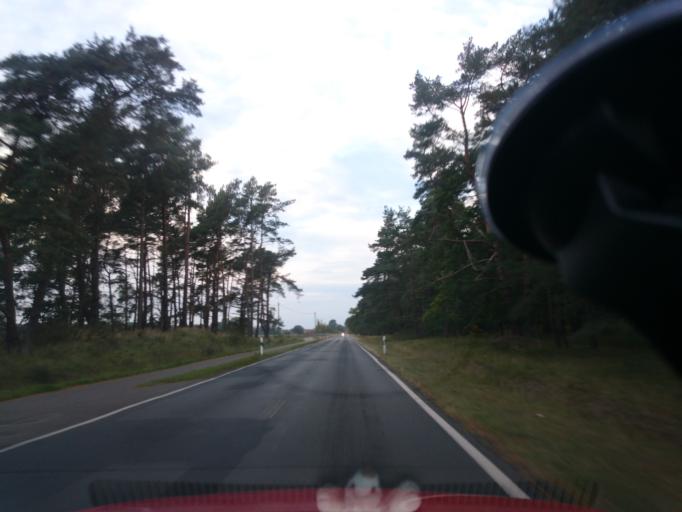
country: DE
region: Mecklenburg-Vorpommern
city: Zingst
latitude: 54.3666
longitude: 12.6369
